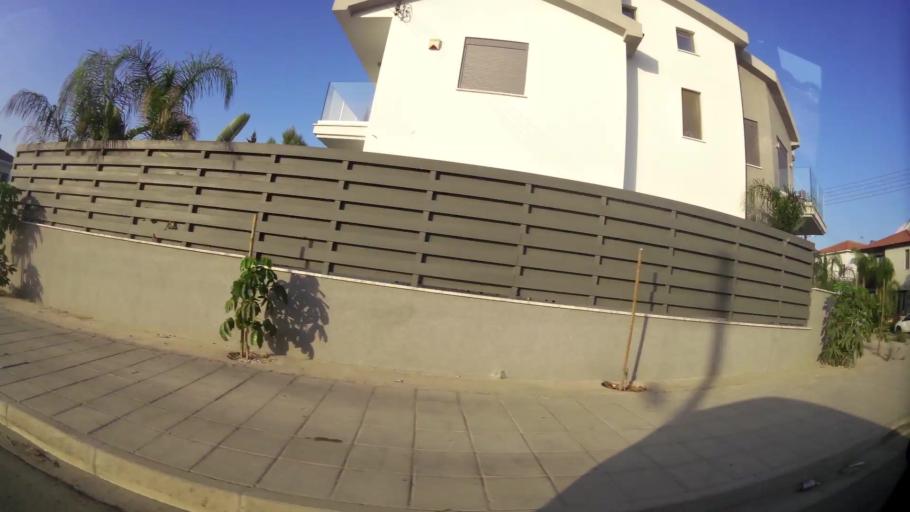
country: CY
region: Larnaka
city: Aradippou
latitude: 34.9290
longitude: 33.5914
